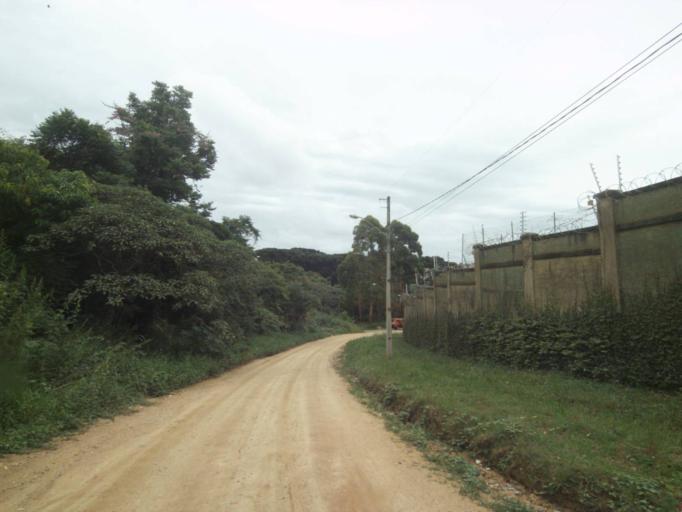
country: BR
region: Parana
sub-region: Curitiba
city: Curitiba
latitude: -25.4572
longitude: -49.3397
